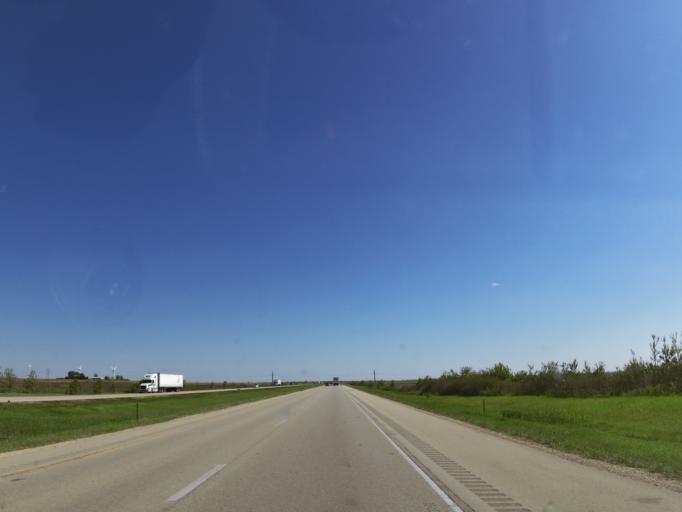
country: US
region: Illinois
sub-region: Ogle County
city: Rochelle
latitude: 41.8323
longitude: -89.0101
